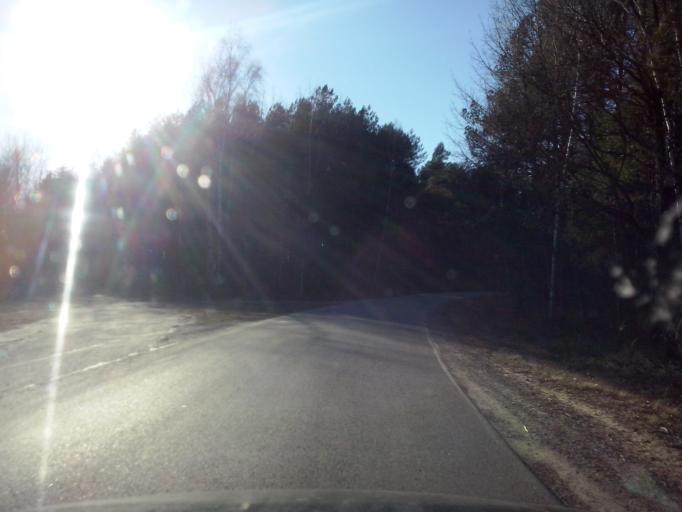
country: PL
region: Subcarpathian Voivodeship
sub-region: Powiat nizanski
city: Harasiuki
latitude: 50.5322
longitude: 22.4521
